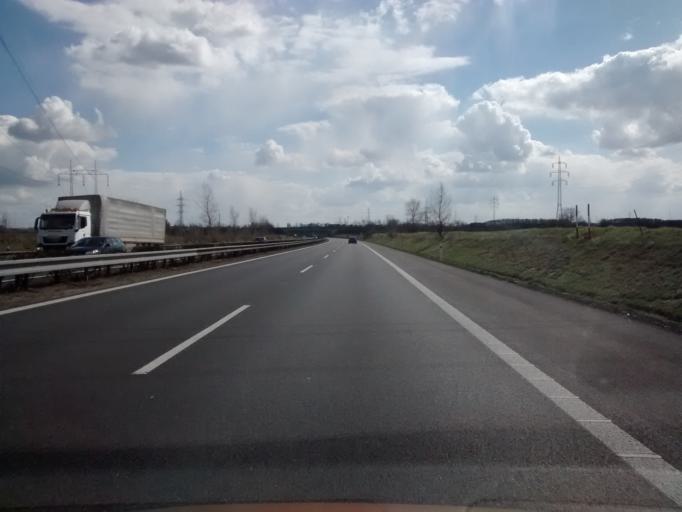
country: CZ
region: Central Bohemia
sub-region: Okres Melnik
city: Veltrusy
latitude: 50.2832
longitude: 14.3524
